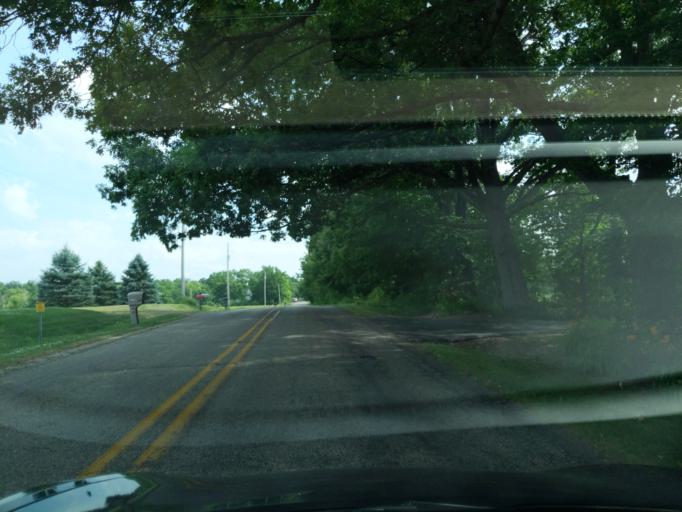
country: US
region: Michigan
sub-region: Eaton County
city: Eaton Rapids
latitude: 42.5279
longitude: -84.6016
